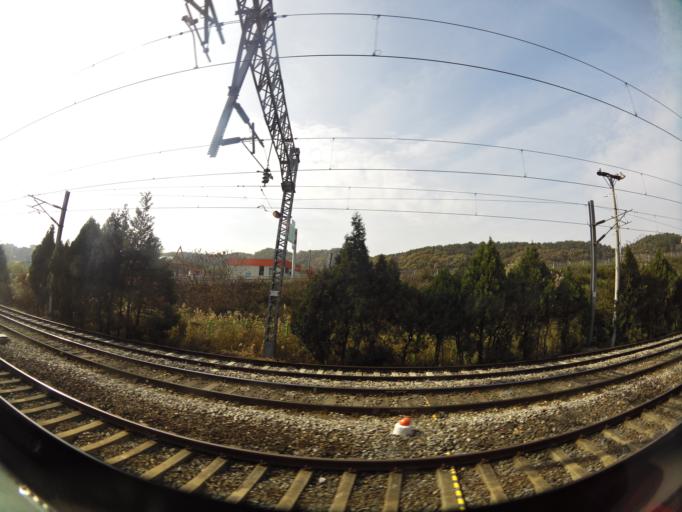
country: KR
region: Chungcheongbuk-do
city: Cheongju-si
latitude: 36.6306
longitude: 127.2896
